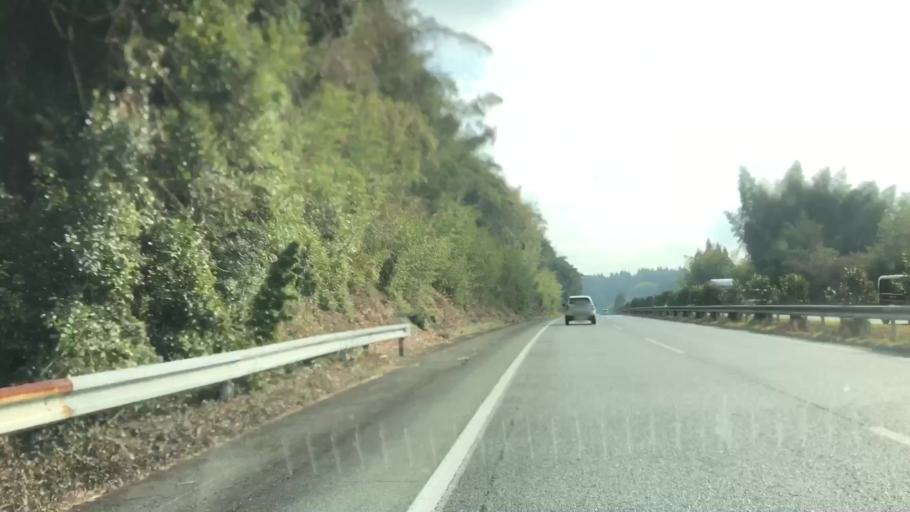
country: JP
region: Kumamoto
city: Yamaga
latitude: 33.0372
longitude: 130.5712
